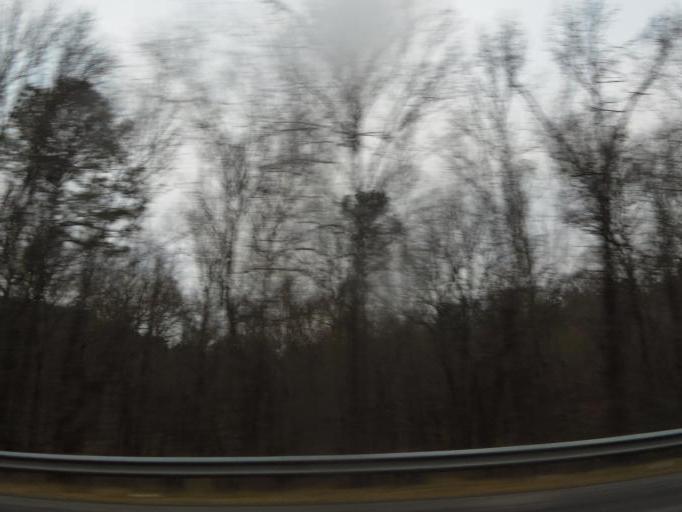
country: US
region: Alabama
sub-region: Blount County
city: Smoke Rise
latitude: 33.8956
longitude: -86.8566
